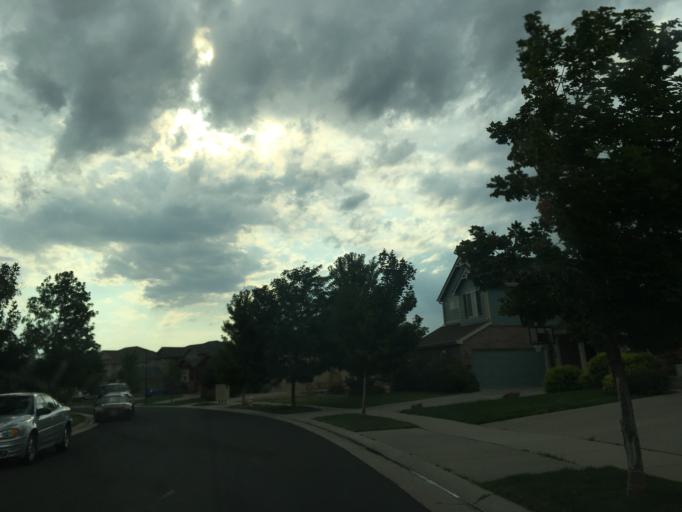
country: US
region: Colorado
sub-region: Douglas County
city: Stonegate
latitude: 39.5114
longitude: -104.8079
